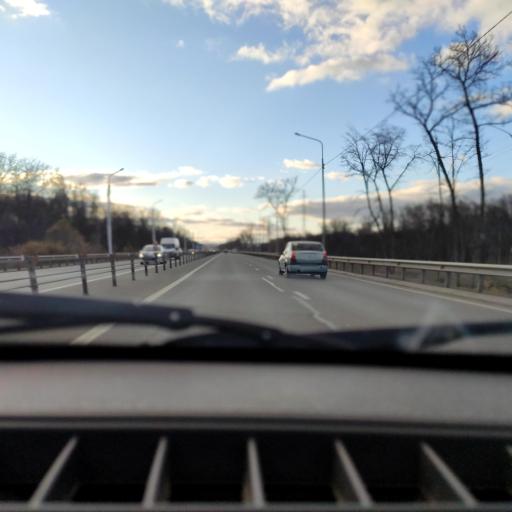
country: RU
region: Bashkortostan
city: Ufa
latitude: 54.6986
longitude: 55.8904
